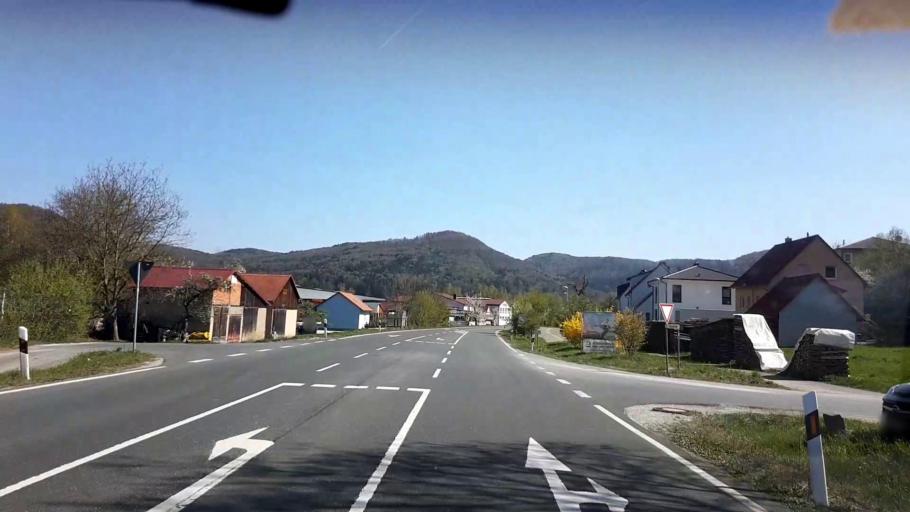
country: DE
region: Bavaria
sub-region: Upper Franconia
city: Unterleinleiter
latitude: 49.8005
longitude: 11.1960
